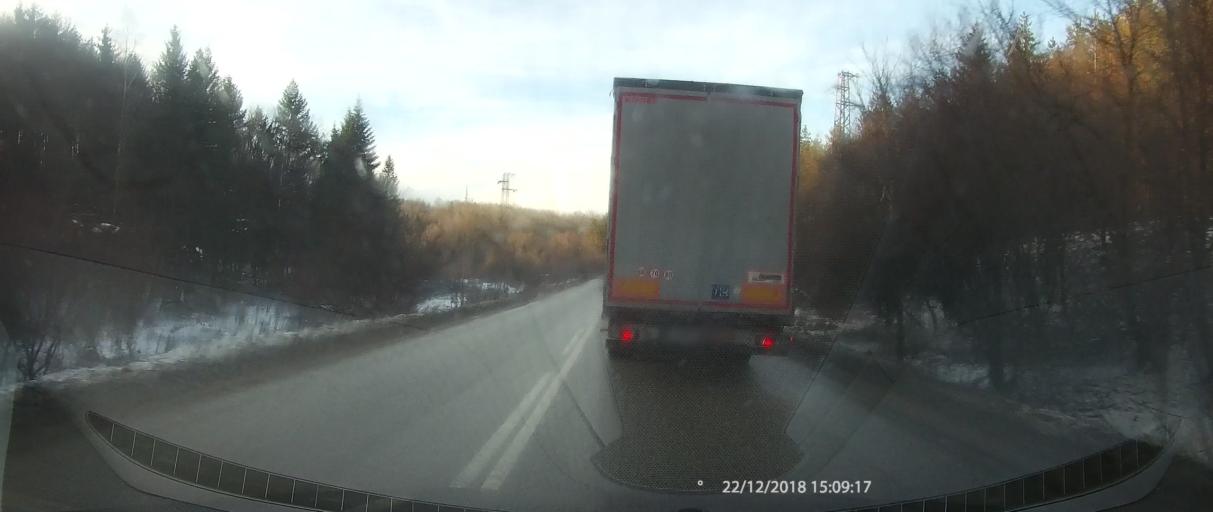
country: BG
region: Ruse
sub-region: Obshtina Borovo
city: Borovo
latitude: 43.5007
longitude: 25.8000
